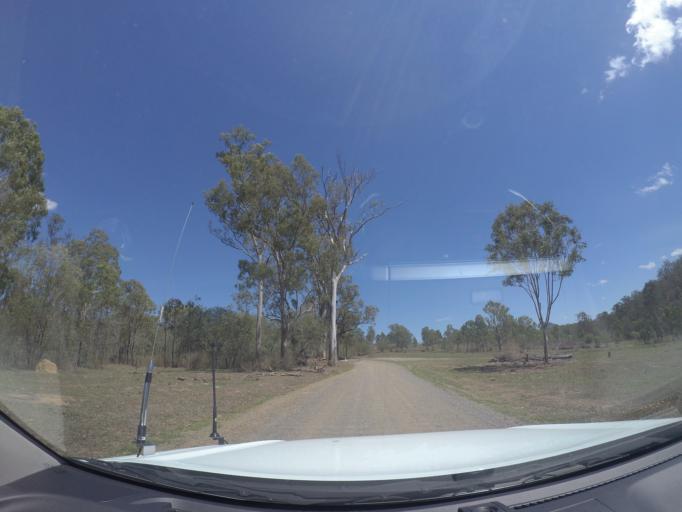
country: AU
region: Queensland
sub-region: Logan
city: Cedar Vale
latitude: -27.8595
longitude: 152.8571
